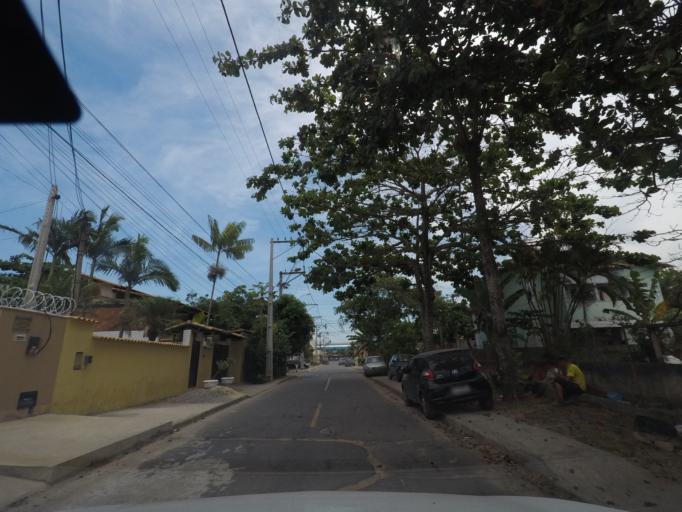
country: BR
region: Rio de Janeiro
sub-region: Marica
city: Marica
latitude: -22.9621
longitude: -42.9599
